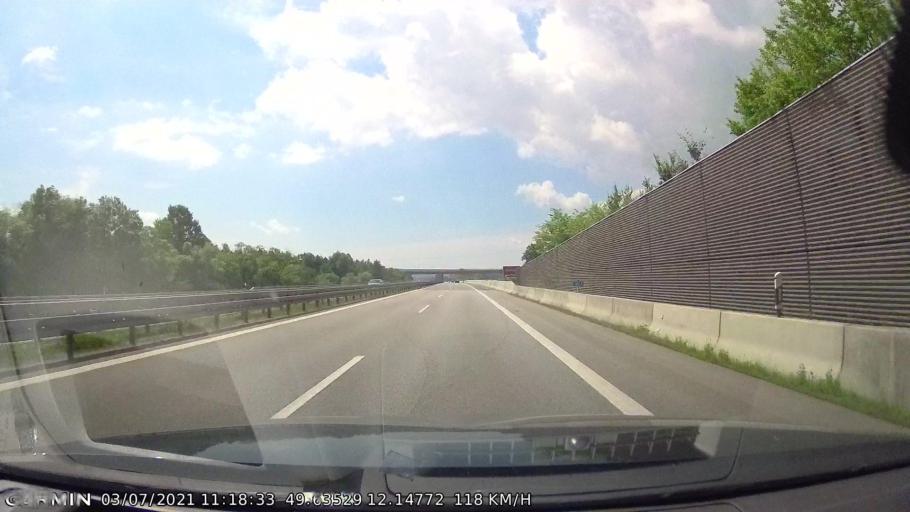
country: DE
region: Bavaria
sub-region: Upper Palatinate
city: Pirk
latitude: 49.6350
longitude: 12.1478
